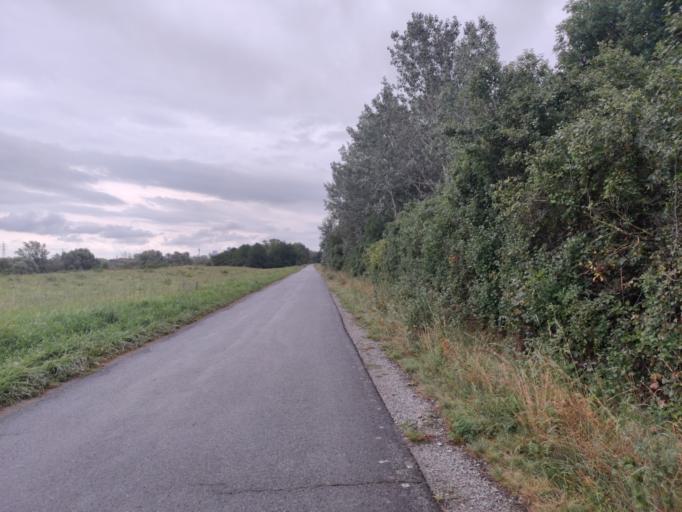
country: AT
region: Lower Austria
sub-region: Politischer Bezirk Korneuburg
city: Langenzersdorf
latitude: 48.2874
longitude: 16.3536
